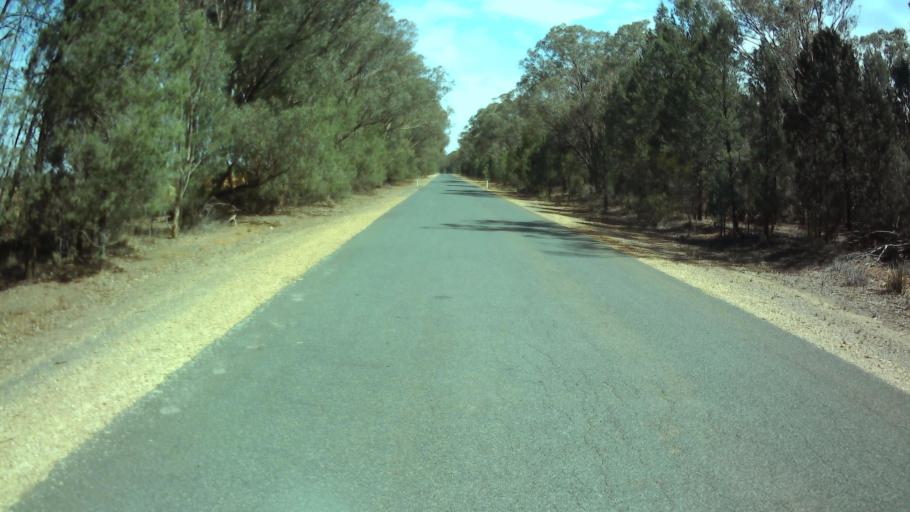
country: AU
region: New South Wales
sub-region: Weddin
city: Grenfell
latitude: -34.0164
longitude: 148.1292
